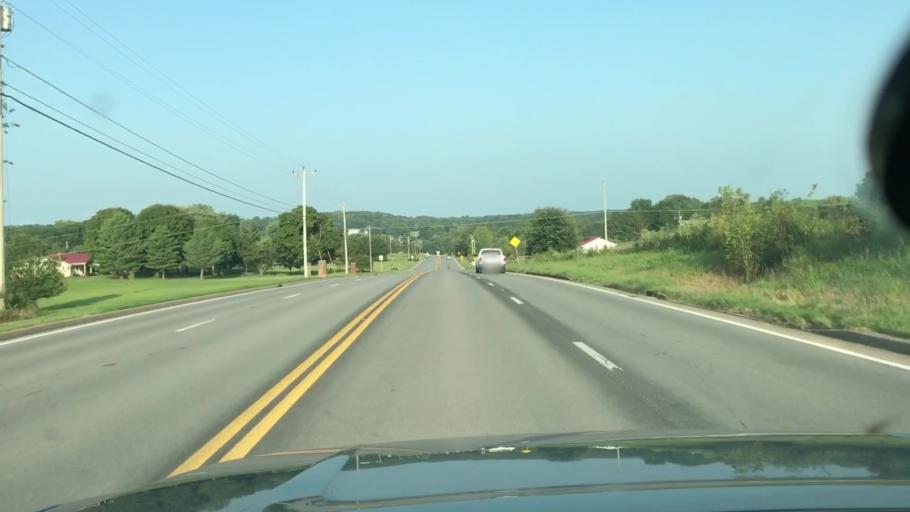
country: US
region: Tennessee
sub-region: Sumner County
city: Portland
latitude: 36.5791
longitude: -86.4700
